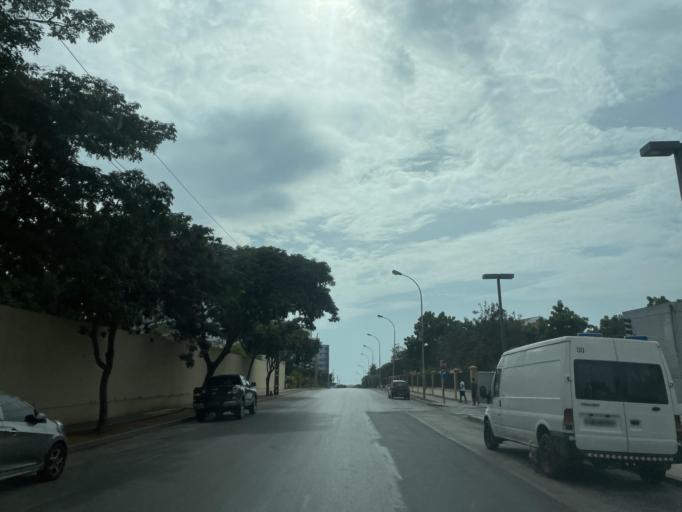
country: AO
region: Luanda
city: Luanda
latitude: -8.9216
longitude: 13.1739
